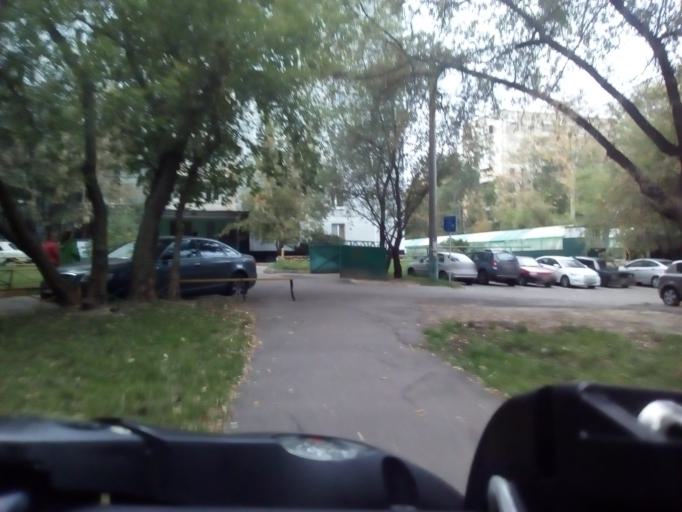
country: RU
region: Moscow
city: Sviblovo
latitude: 55.8548
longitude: 37.6399
